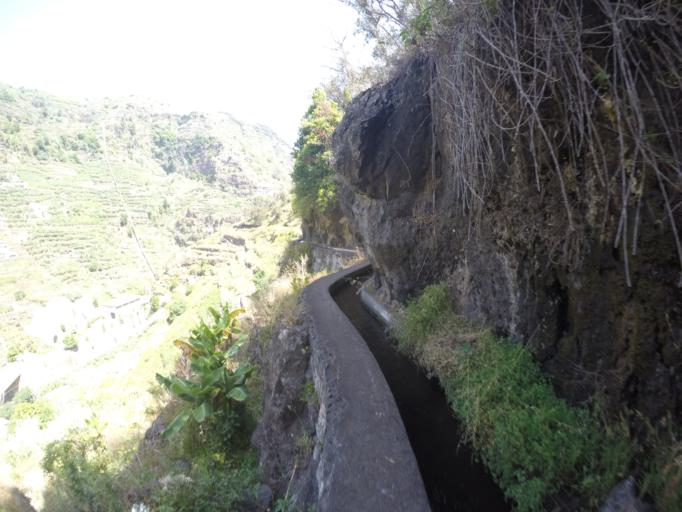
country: PT
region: Madeira
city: Camara de Lobos
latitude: 32.6653
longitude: -16.9588
